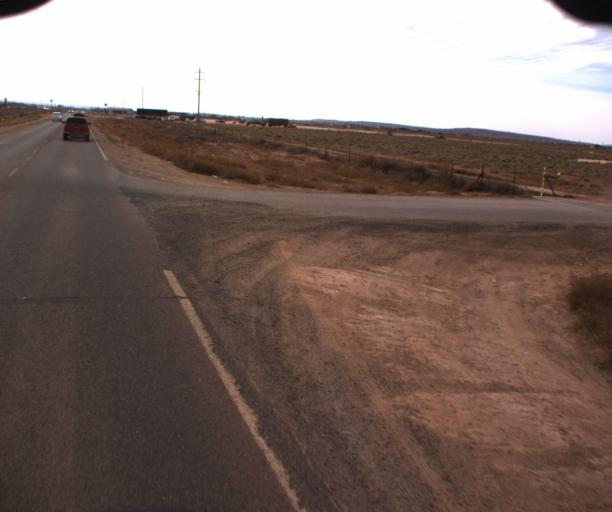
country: US
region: Arizona
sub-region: Apache County
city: Chinle
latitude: 36.1728
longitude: -109.5877
